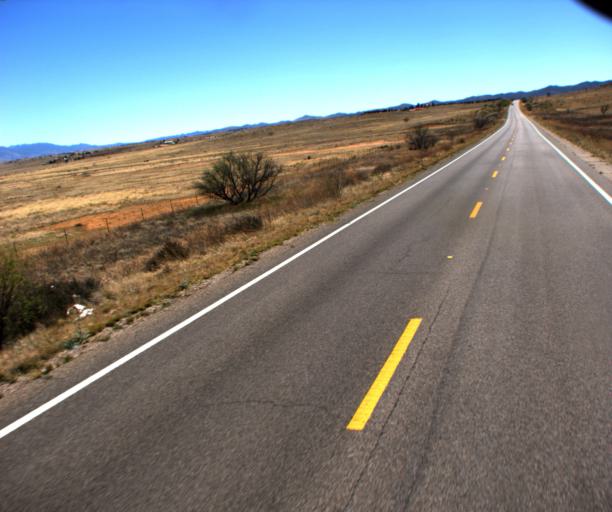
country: US
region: Arizona
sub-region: Pima County
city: Corona de Tucson
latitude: 31.7079
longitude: -110.6555
